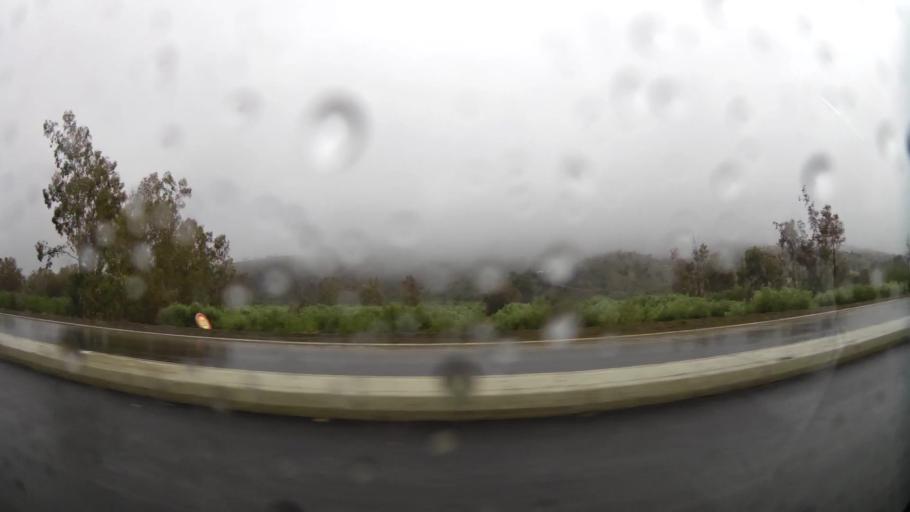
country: MA
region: Taza-Al Hoceima-Taounate
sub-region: Taza
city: Aknoul
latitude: 34.8011
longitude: -3.7407
